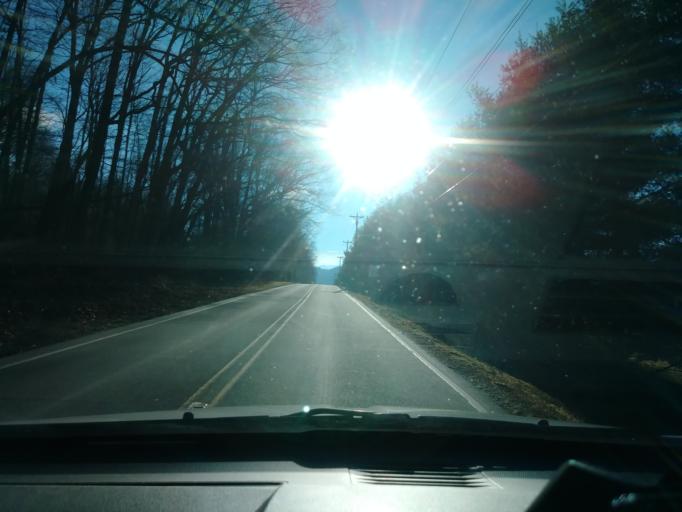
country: US
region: North Carolina
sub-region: Avery County
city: Banner Elk
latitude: 36.1642
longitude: -81.9018
